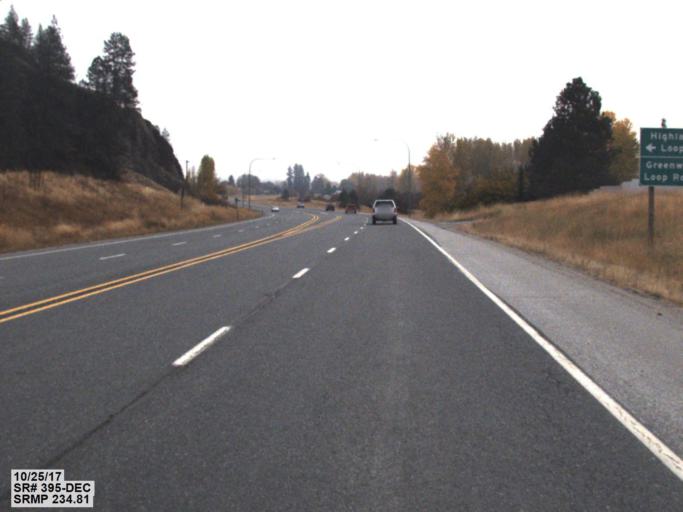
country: US
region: Washington
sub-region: Stevens County
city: Kettle Falls
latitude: 48.5901
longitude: -117.9924
